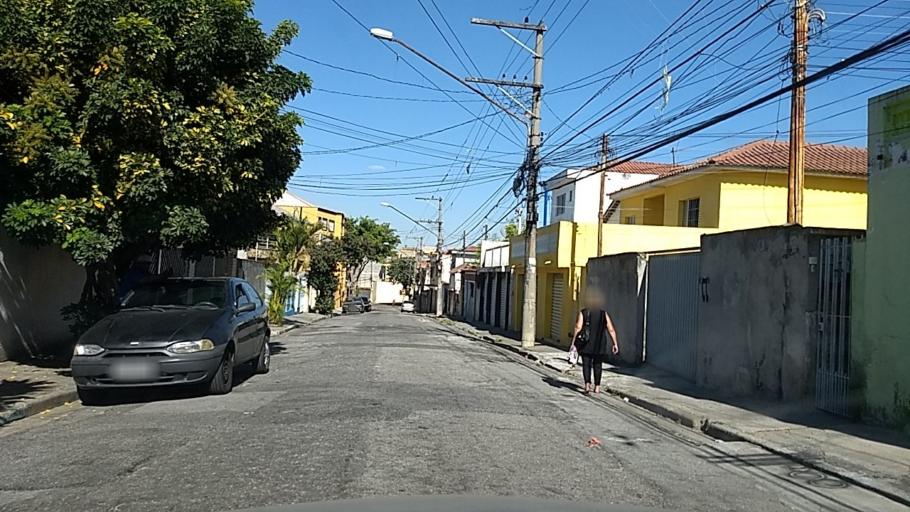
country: BR
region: Sao Paulo
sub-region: Guarulhos
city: Guarulhos
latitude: -23.4964
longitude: -46.5783
